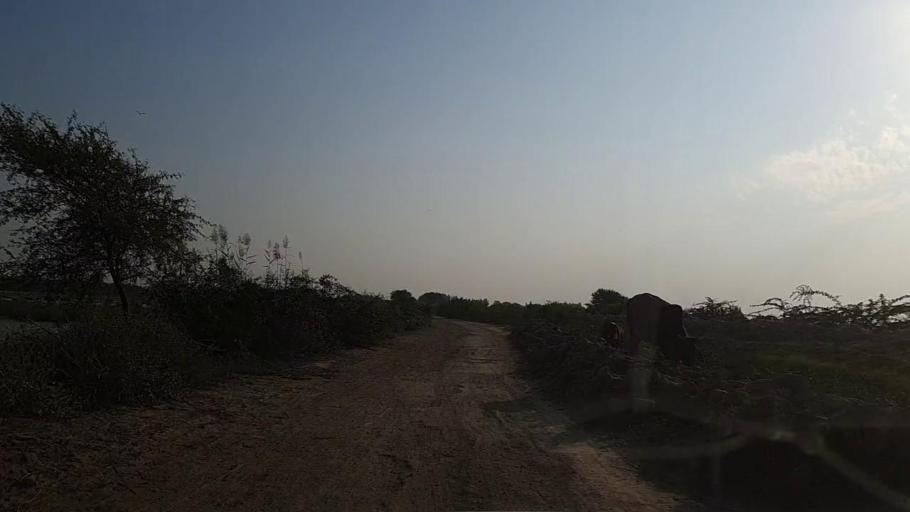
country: PK
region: Sindh
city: Mirpur Batoro
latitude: 24.7704
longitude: 68.2348
